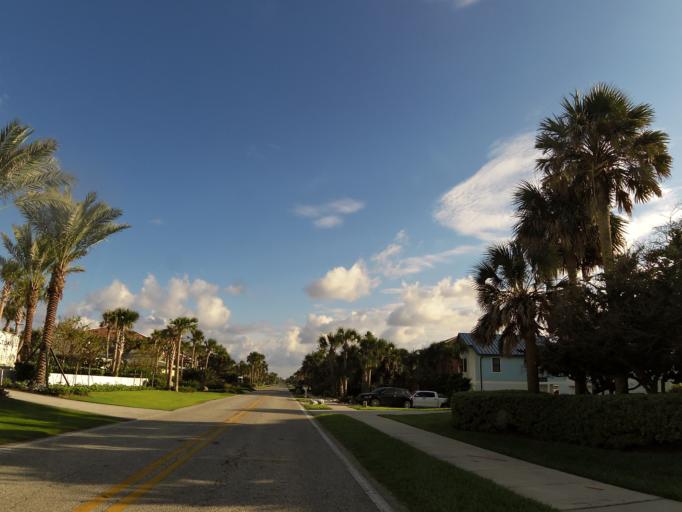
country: US
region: Florida
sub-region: Saint Johns County
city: Sawgrass
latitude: 30.2079
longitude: -81.3692
